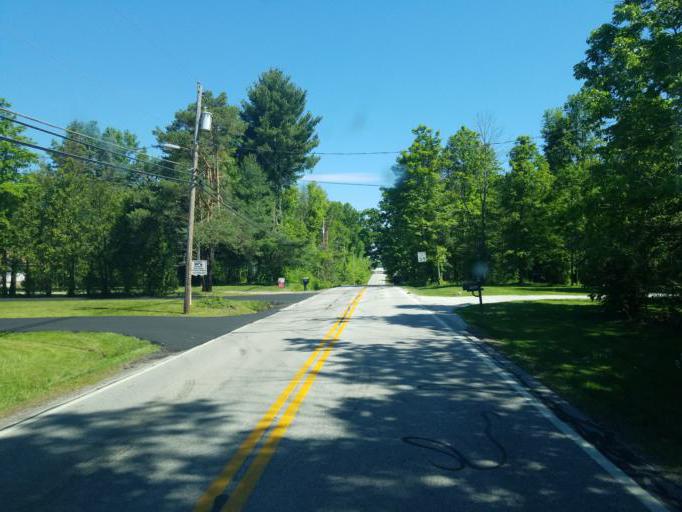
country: US
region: Ohio
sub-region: Summit County
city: Boston Heights
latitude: 41.2658
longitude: -81.4895
